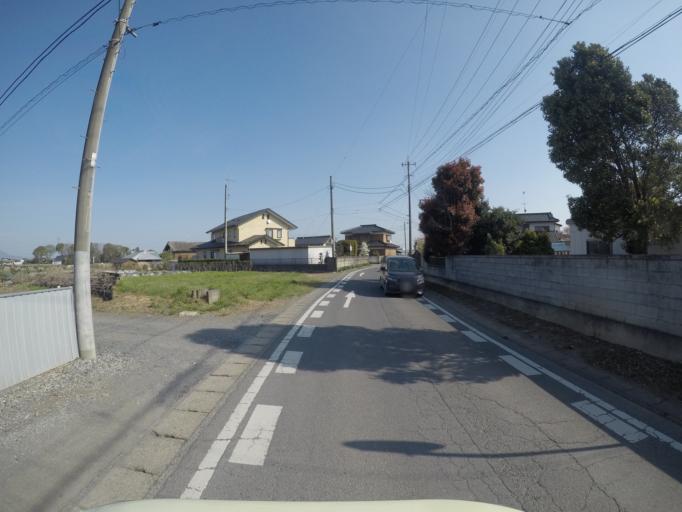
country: JP
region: Ibaraki
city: Yuki
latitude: 36.2361
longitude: 139.8774
